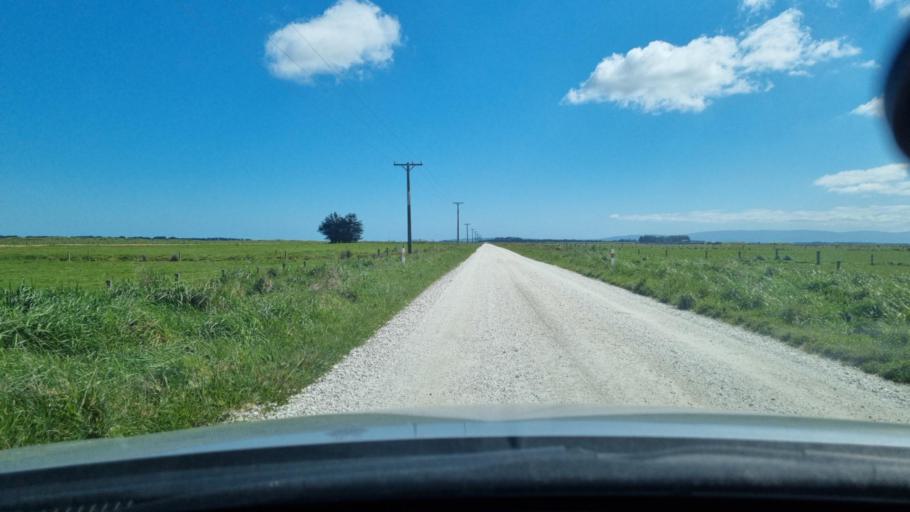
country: NZ
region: Southland
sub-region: Invercargill City
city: Invercargill
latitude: -46.3693
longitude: 168.2747
